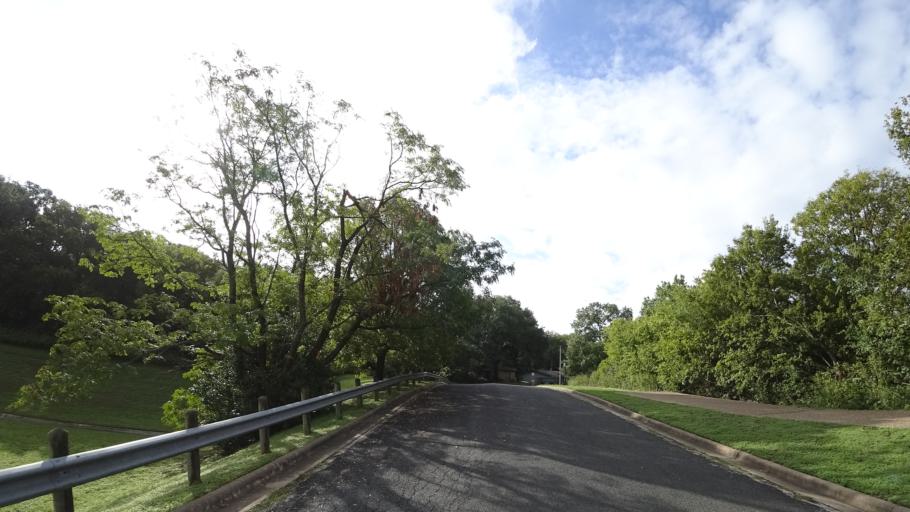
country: US
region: Texas
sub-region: Travis County
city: West Lake Hills
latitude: 30.3467
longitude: -97.7448
